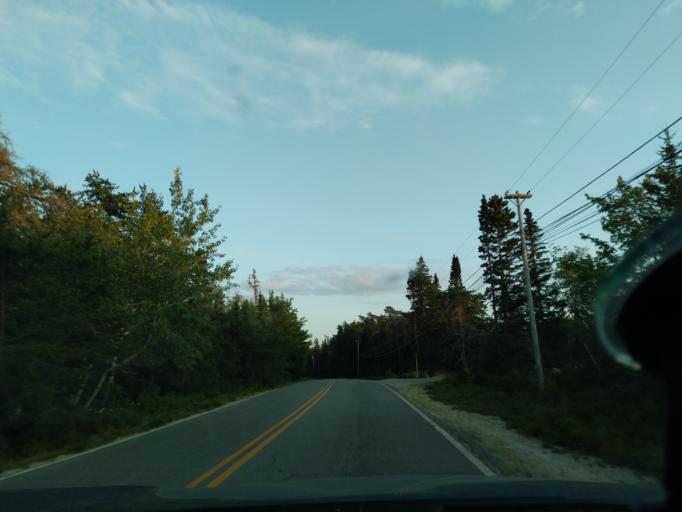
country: US
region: Maine
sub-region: Hancock County
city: Gouldsboro
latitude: 44.3787
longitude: -68.0363
